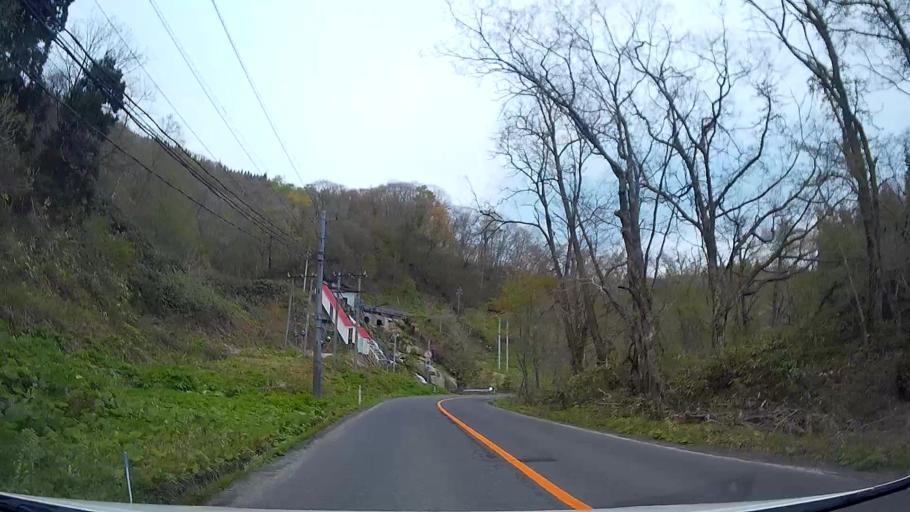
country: JP
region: Akita
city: Hanawa
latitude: 40.3737
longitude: 140.8795
